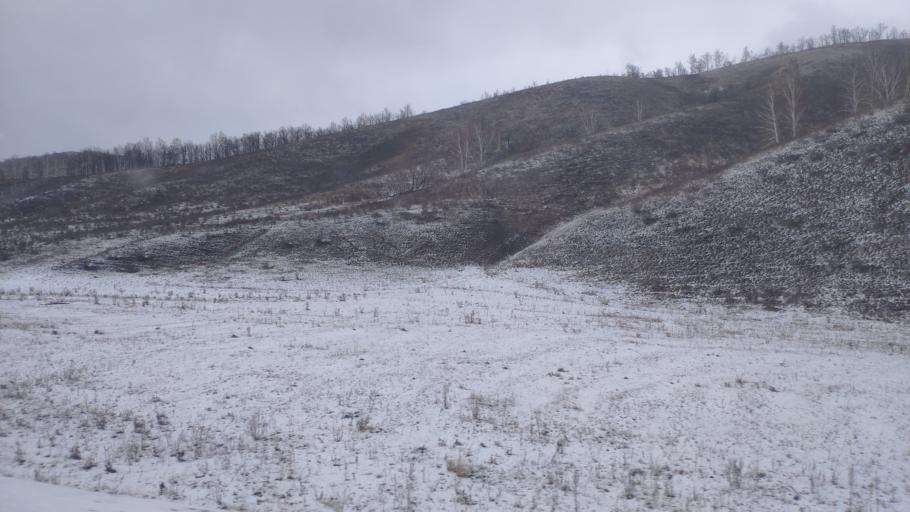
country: RU
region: Bashkortostan
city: Isyangulovo
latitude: 52.1616
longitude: 56.9123
